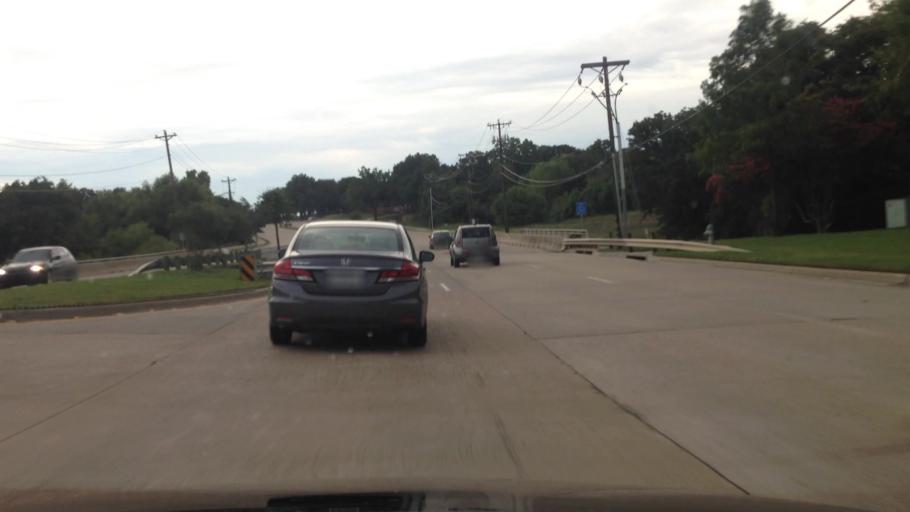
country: US
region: Texas
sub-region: Denton County
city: Flower Mound
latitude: 33.0072
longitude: -97.0452
